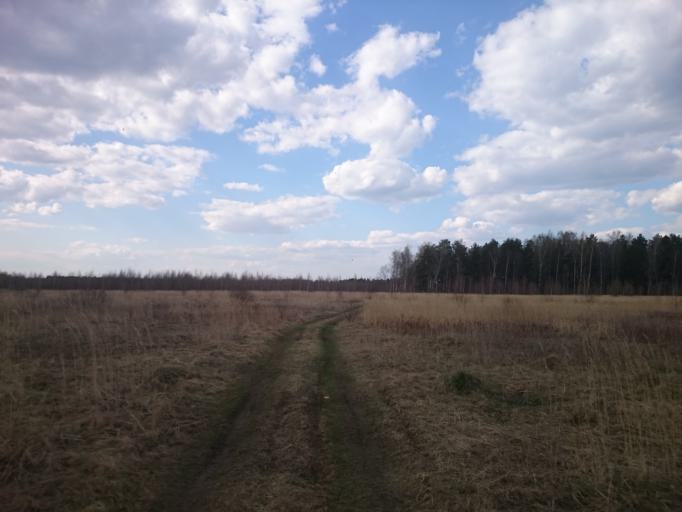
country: RU
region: Moskovskaya
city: Klin
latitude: 56.3964
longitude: 36.6825
